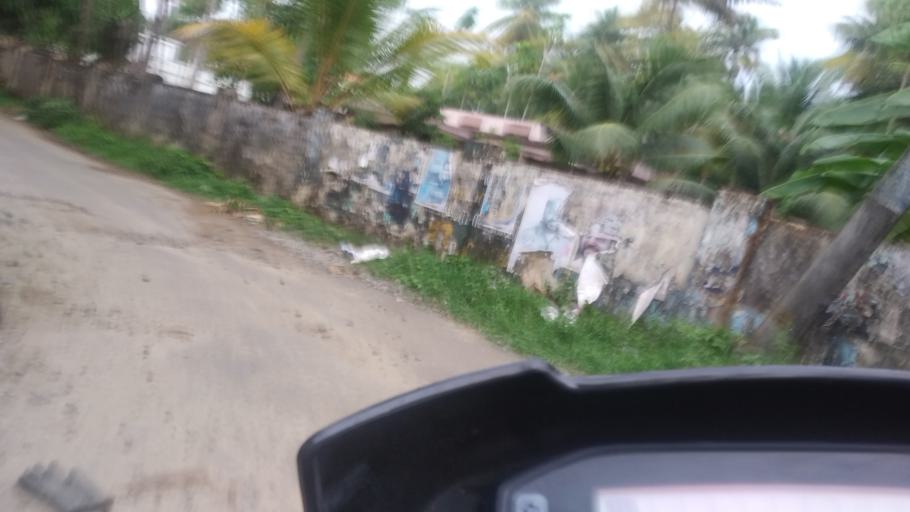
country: IN
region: Kerala
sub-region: Ernakulam
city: Elur
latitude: 10.0672
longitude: 76.2171
